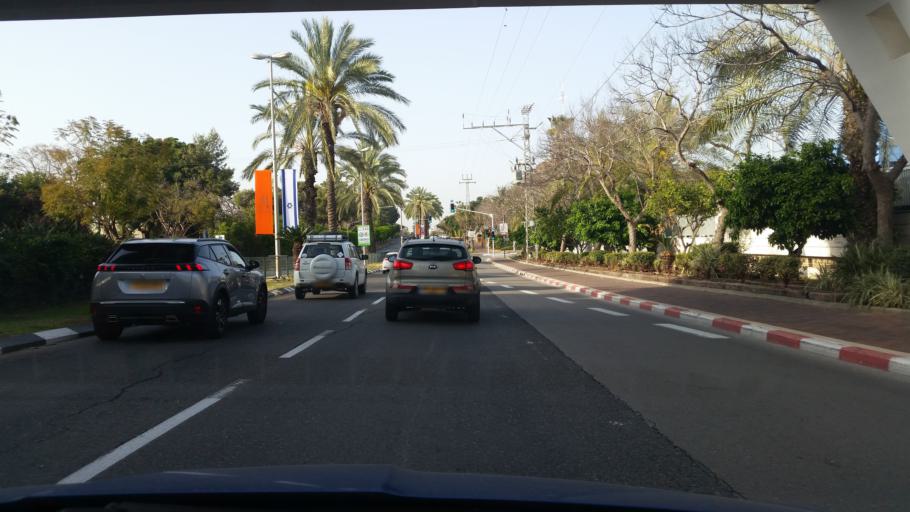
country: IL
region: Central District
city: Ra'anana
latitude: 32.1864
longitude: 34.8544
